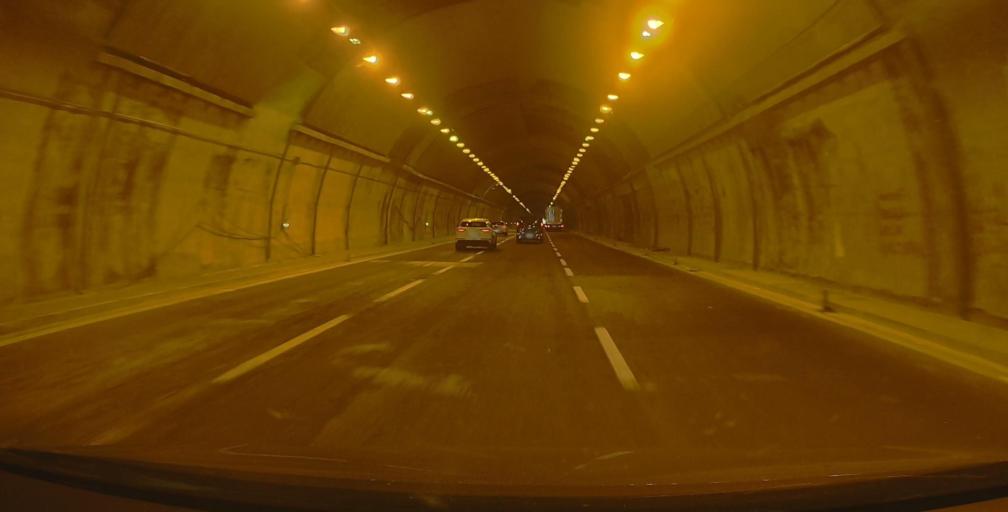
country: IT
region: Campania
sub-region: Provincia di Salerno
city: Nocera Inferiore
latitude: 40.7740
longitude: 14.6517
